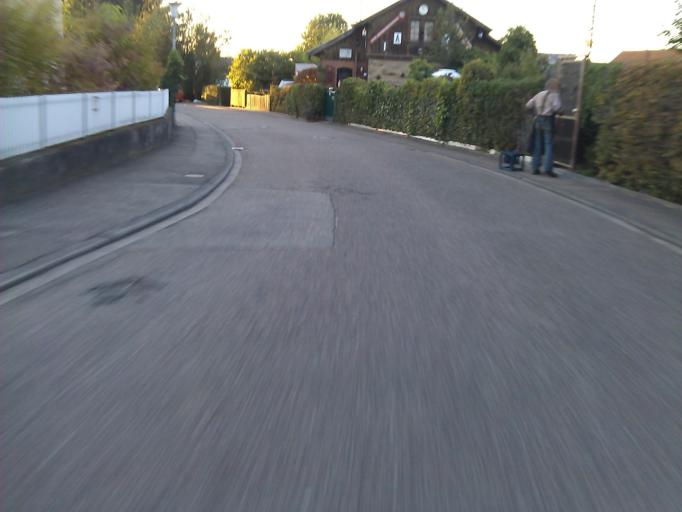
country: DE
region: Baden-Wuerttemberg
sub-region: Karlsruhe Region
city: Sinsheim
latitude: 49.2384
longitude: 8.9050
